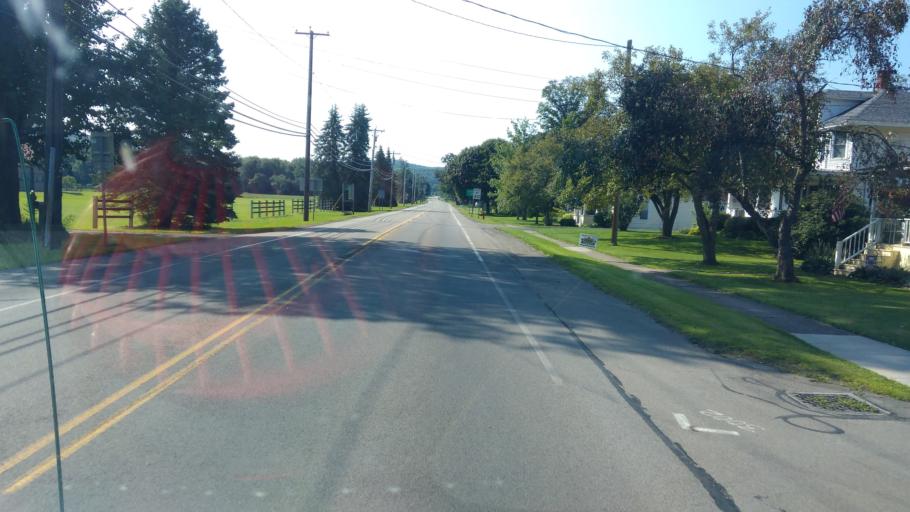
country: US
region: New York
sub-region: Allegany County
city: Cuba
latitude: 42.2113
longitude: -78.2752
